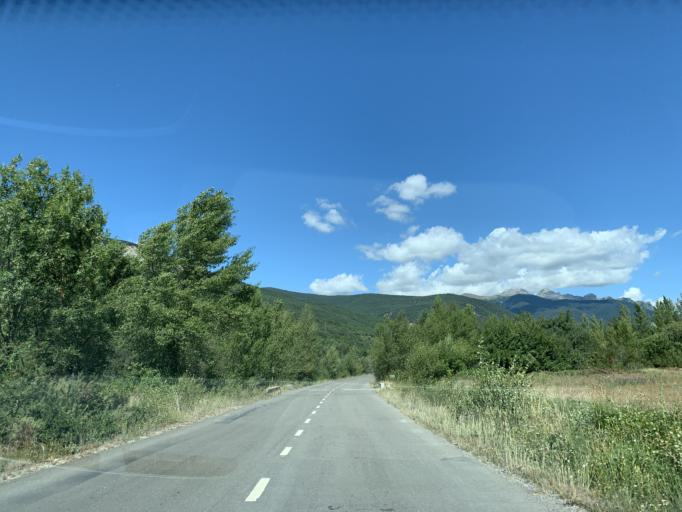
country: ES
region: Aragon
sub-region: Provincia de Huesca
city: Biescas
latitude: 42.5727
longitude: -0.3188
